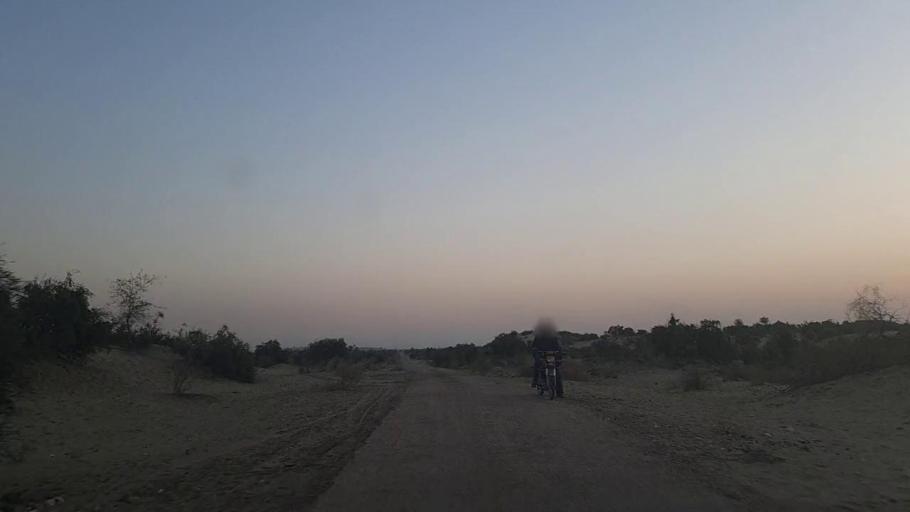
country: PK
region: Sindh
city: Jam Sahib
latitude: 26.4150
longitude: 68.8094
